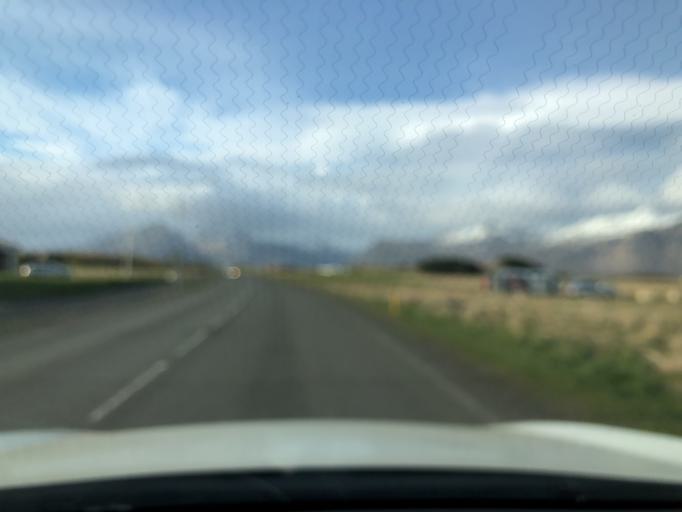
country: IS
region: East
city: Hoefn
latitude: 64.2633
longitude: -15.2020
